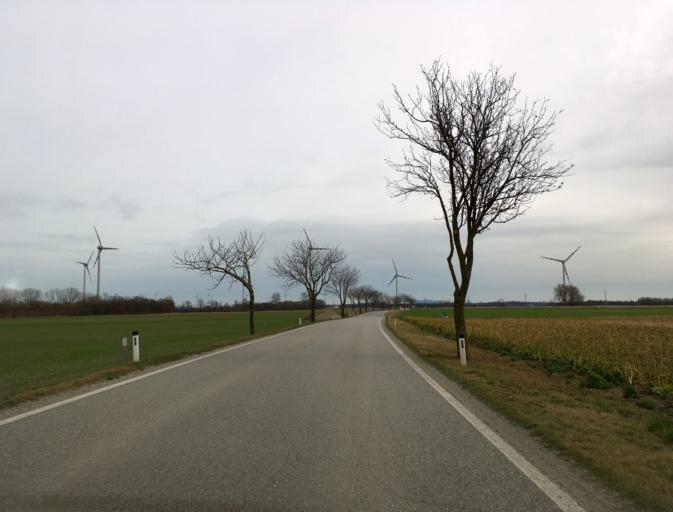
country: AT
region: Lower Austria
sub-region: Politischer Bezirk Ganserndorf
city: Glinzendorf
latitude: 48.2458
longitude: 16.6551
